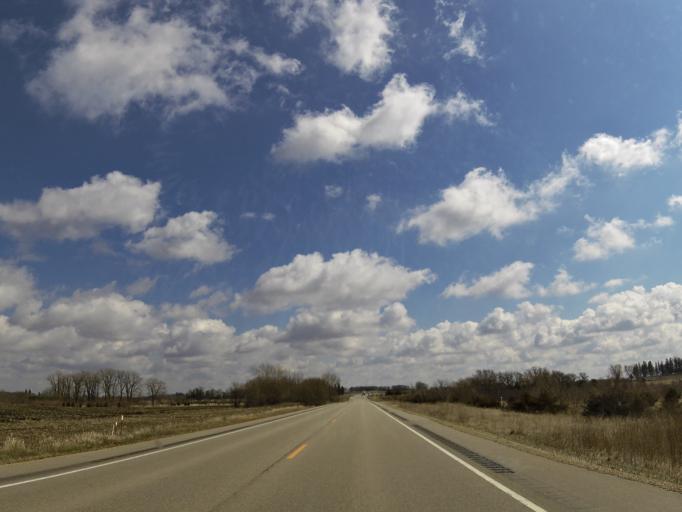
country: US
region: Minnesota
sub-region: Goodhue County
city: Kenyon
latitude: 44.1813
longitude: -92.9103
